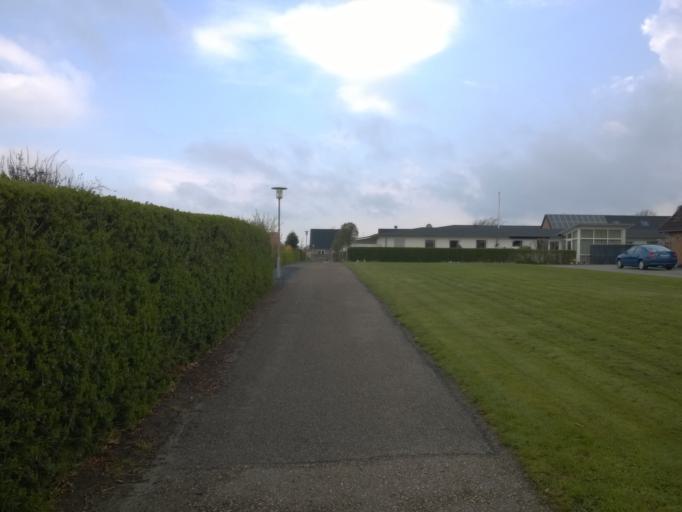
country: DK
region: Central Jutland
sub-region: Holstebro Kommune
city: Vinderup
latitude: 56.4758
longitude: 8.7747
